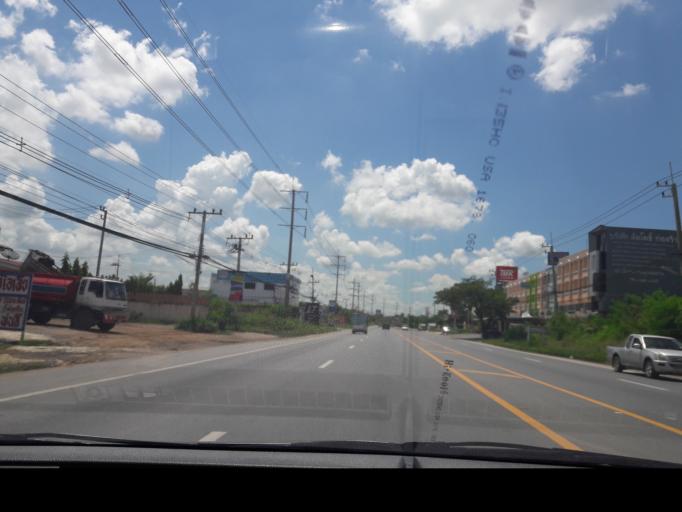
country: TH
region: Nakhon Pathom
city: Kamphaeng Saen
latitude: 14.0111
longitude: 100.0076
